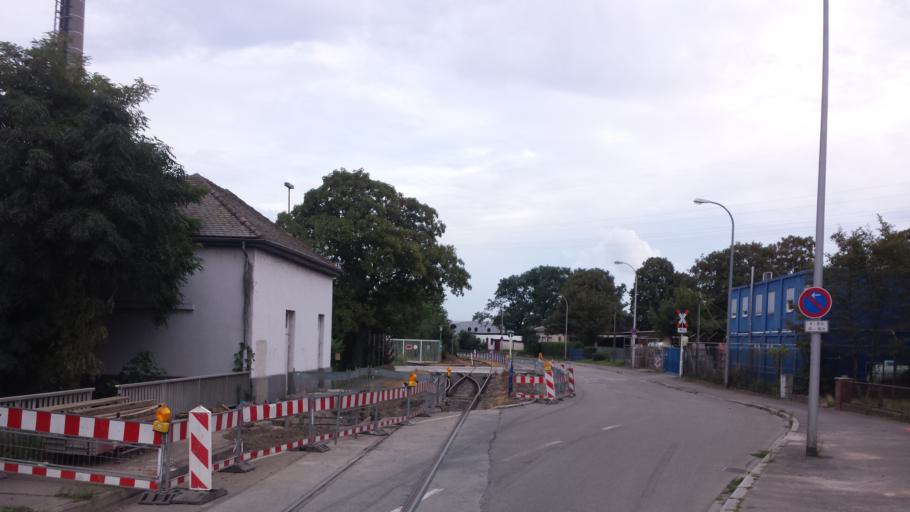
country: DE
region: Rheinland-Pfalz
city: Ludwigshafen am Rhein
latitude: 49.5071
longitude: 8.4484
